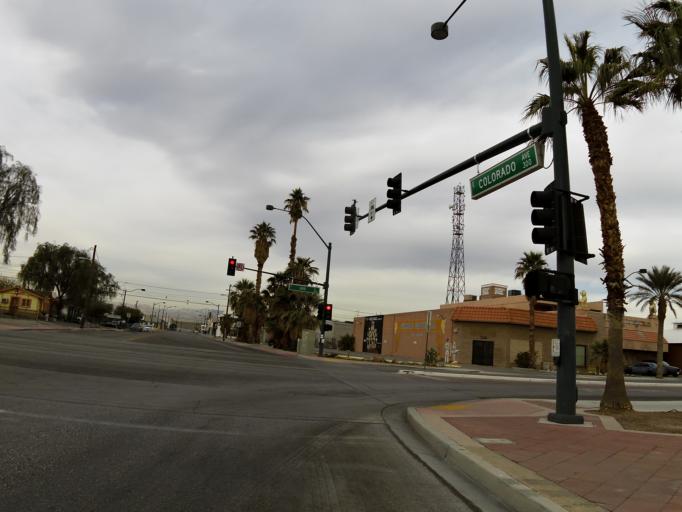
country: US
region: Nevada
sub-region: Clark County
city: Las Vegas
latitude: 36.1560
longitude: -115.1509
